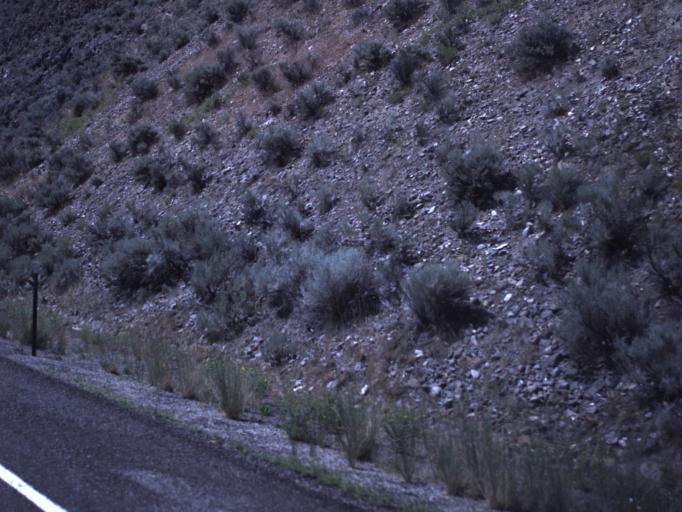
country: US
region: Utah
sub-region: Piute County
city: Junction
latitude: 38.1079
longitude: -112.3362
